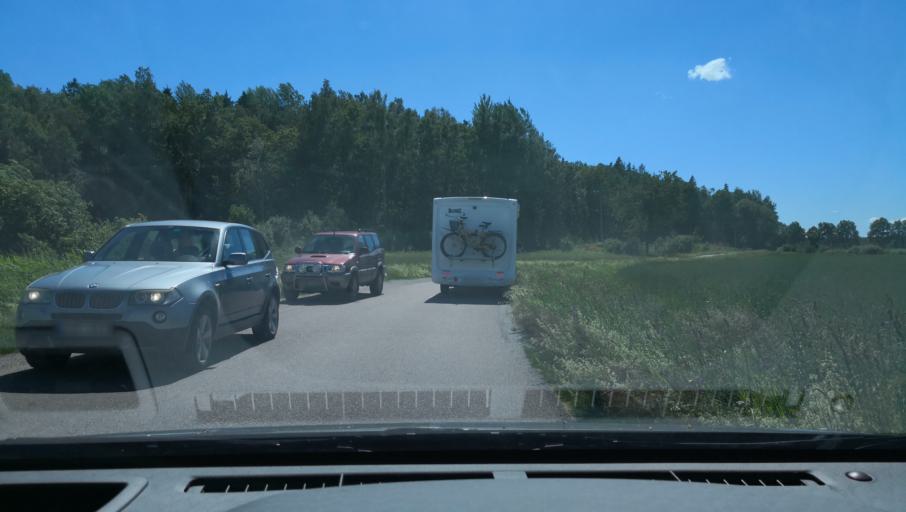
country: SE
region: Vaestmanland
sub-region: Arboga Kommun
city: Tyringe
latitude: 59.4010
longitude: 15.9371
